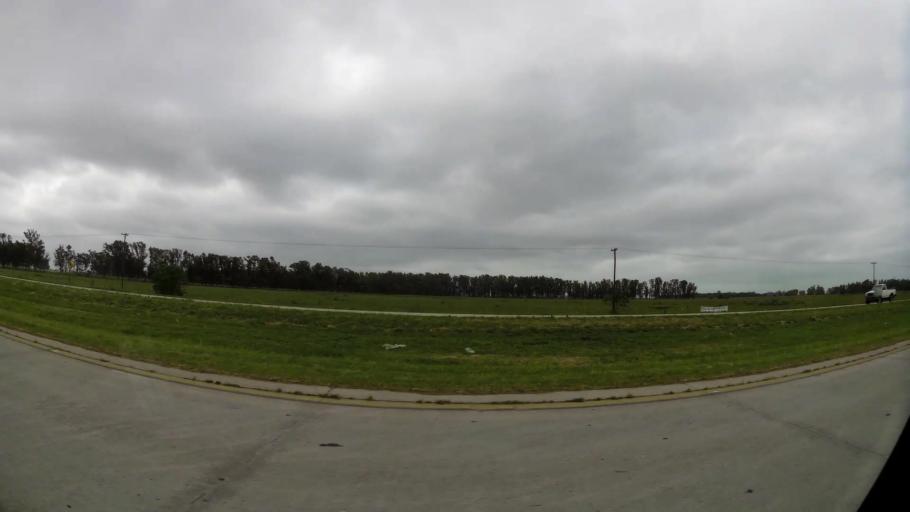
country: AR
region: Buenos Aires
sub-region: Partido de San Vicente
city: San Vicente
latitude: -35.0187
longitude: -58.2709
